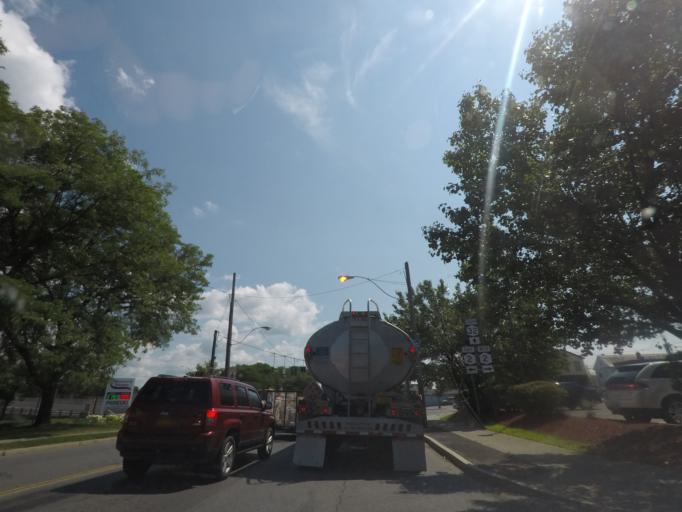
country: US
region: New York
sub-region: Albany County
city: Watervliet
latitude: 42.7306
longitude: -73.7015
